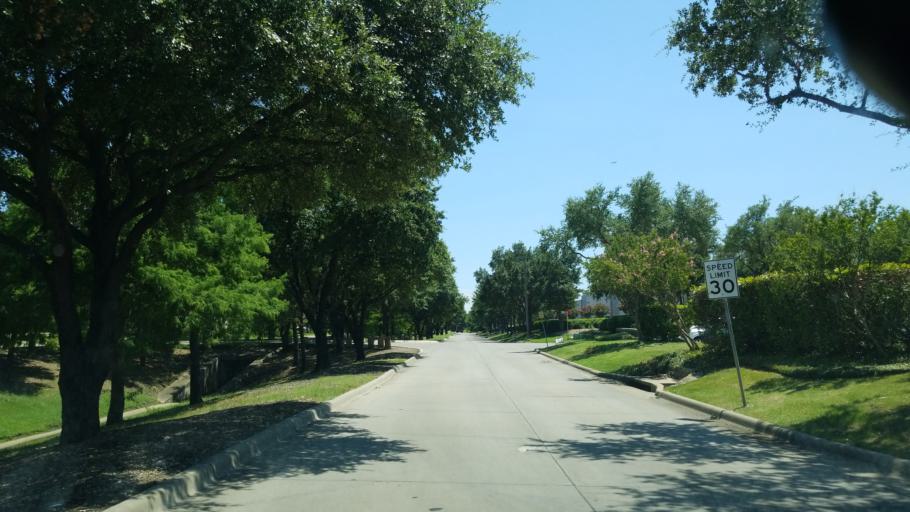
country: US
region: Texas
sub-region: Dallas County
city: Farmers Branch
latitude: 32.9303
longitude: -96.9153
